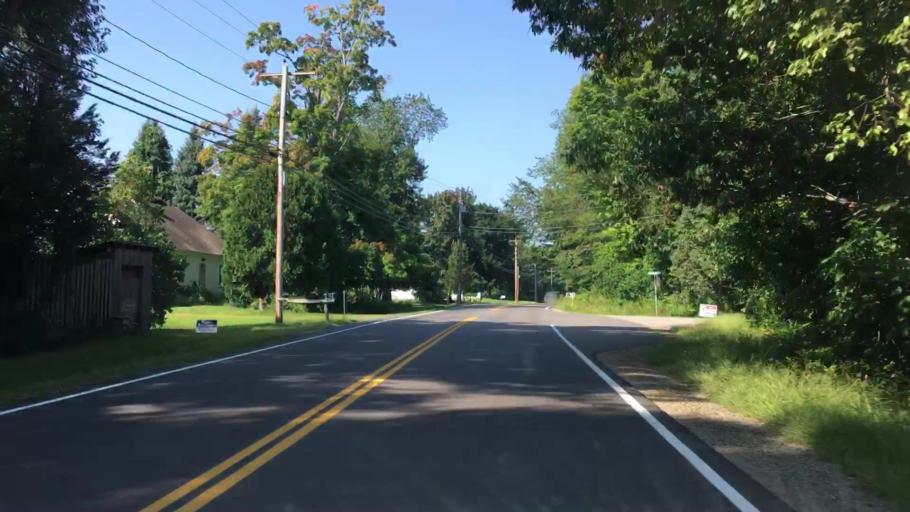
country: US
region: New Hampshire
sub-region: Rockingham County
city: East Kingston
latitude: 42.9299
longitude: -71.0294
